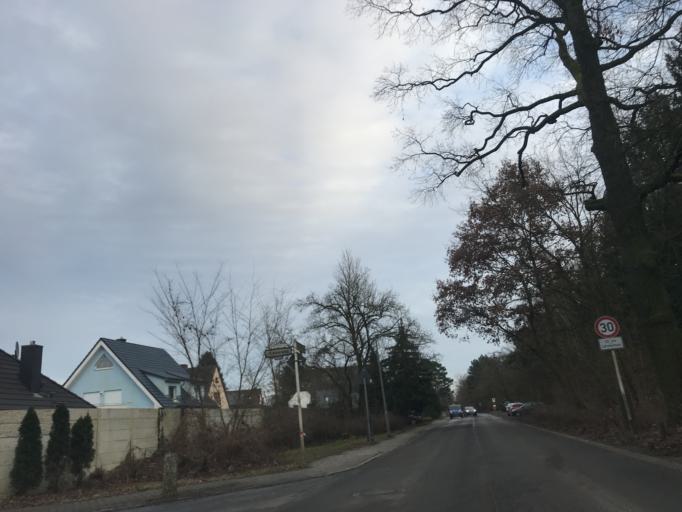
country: DE
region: Berlin
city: Falkenhagener Feld
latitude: 52.5600
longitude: 13.1750
